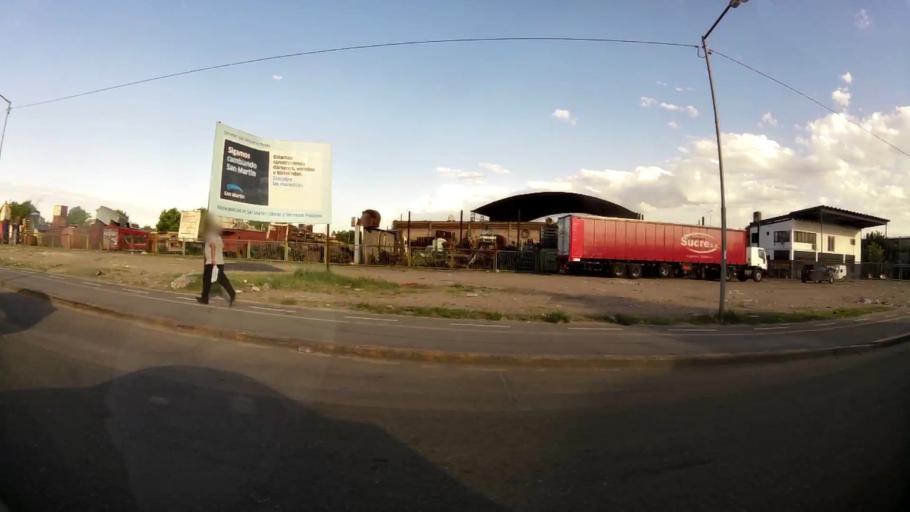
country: AR
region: Buenos Aires
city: Caseros
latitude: -34.5544
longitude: -58.5851
